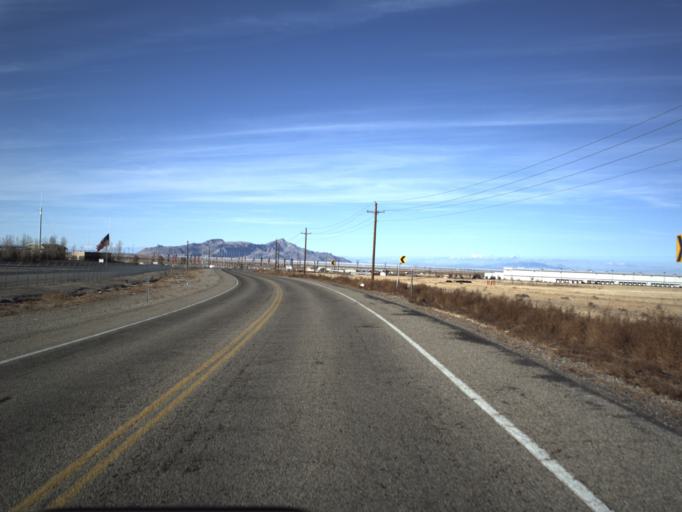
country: US
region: Utah
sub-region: Tooele County
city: Erda
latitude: 40.5786
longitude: -112.3678
